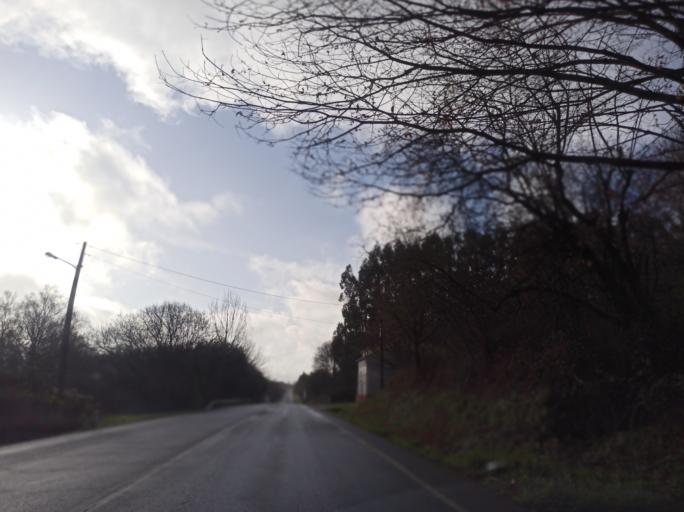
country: ES
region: Galicia
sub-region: Provincia da Coruna
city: Curtis
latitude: 43.0870
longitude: -8.0158
